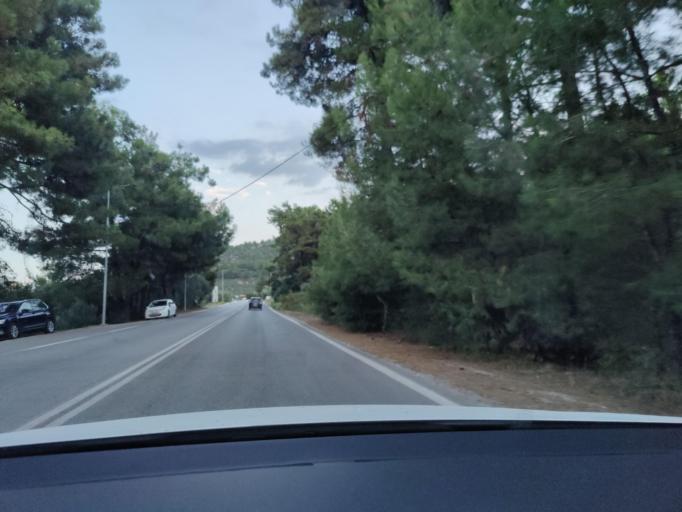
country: GR
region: East Macedonia and Thrace
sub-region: Nomos Kavalas
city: Prinos
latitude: 40.7888
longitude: 24.6284
